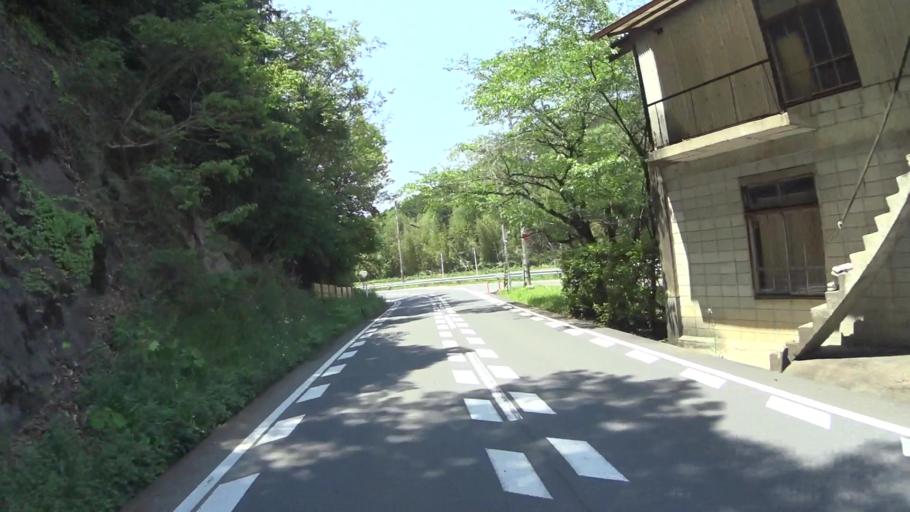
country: JP
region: Kyoto
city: Kameoka
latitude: 35.0762
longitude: 135.5450
